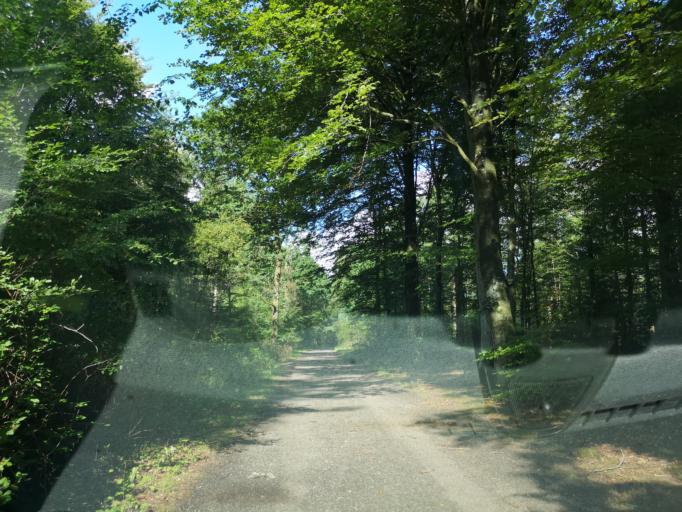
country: DK
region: Central Jutland
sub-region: Holstebro Kommune
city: Holstebro
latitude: 56.3359
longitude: 8.6329
